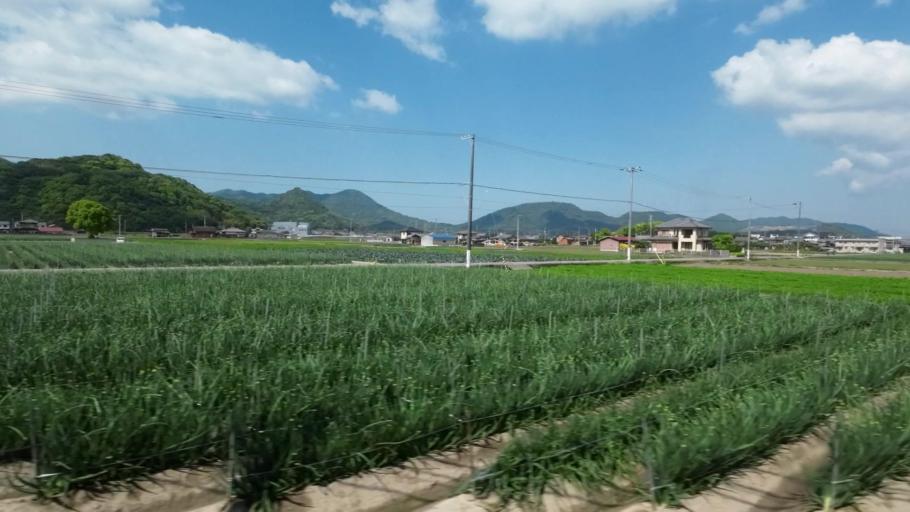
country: JP
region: Kagawa
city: Tadotsu
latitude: 34.2003
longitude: 133.7128
